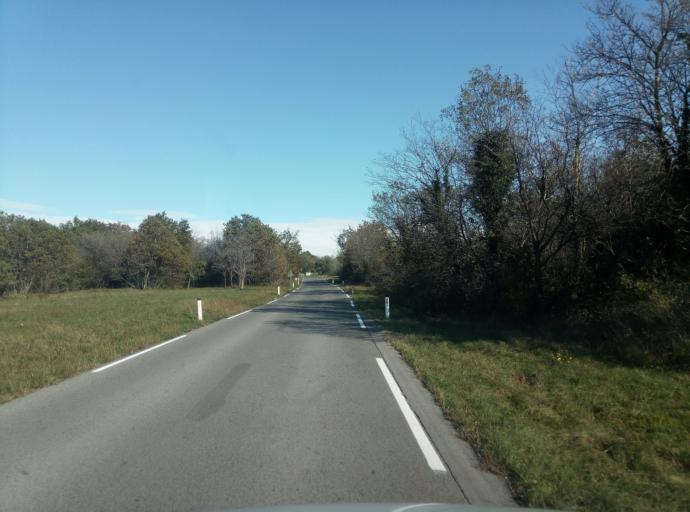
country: SI
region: Komen
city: Komen
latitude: 45.8127
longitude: 13.7331
